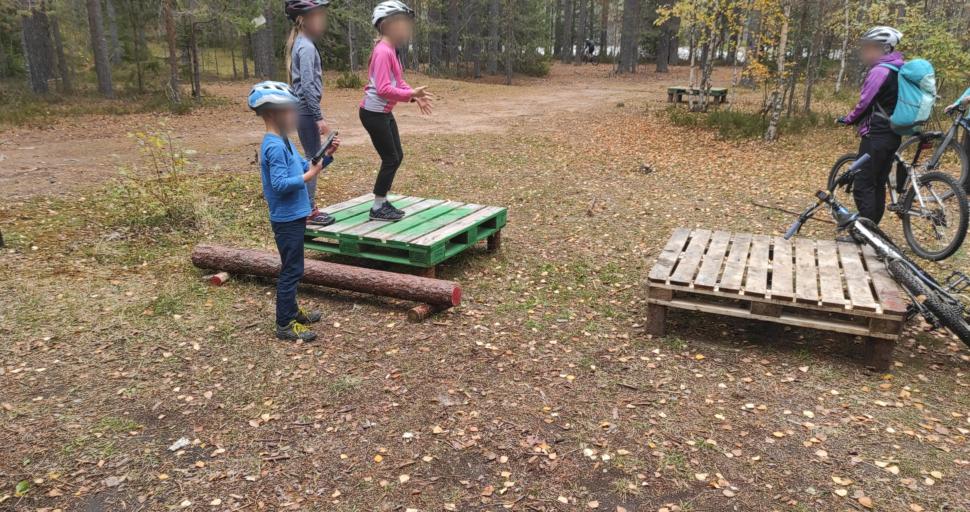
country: RU
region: Leningrad
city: Sosnovyy Bor
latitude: 60.2180
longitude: 29.1446
